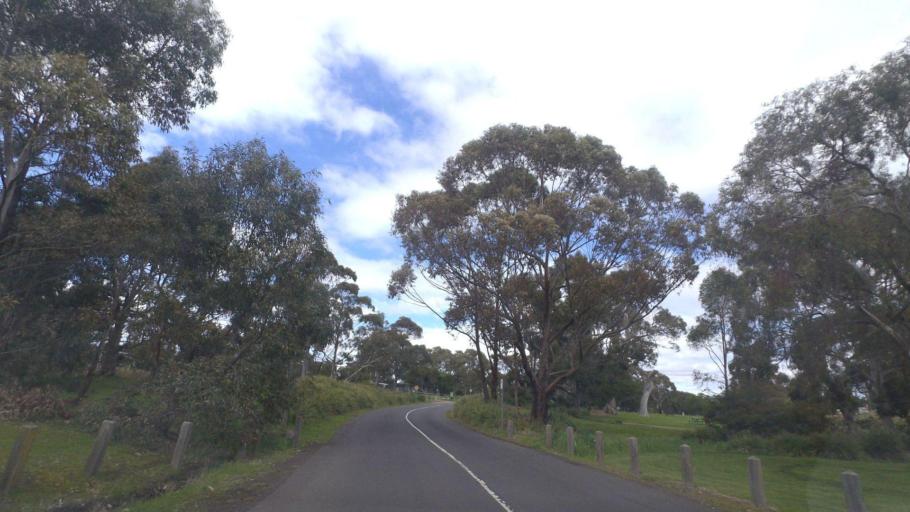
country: AU
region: Victoria
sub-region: Darebin
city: Kingsbury
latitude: -37.7076
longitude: 145.0453
